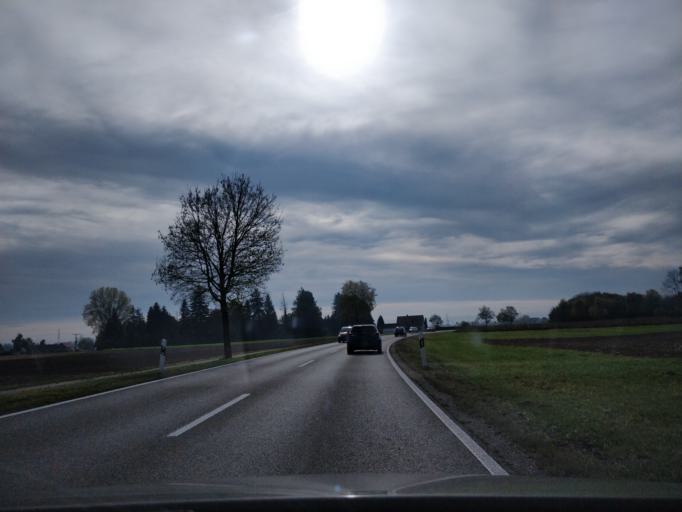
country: DE
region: Bavaria
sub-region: Swabia
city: Konigsbrunn
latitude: 48.2548
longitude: 10.9054
